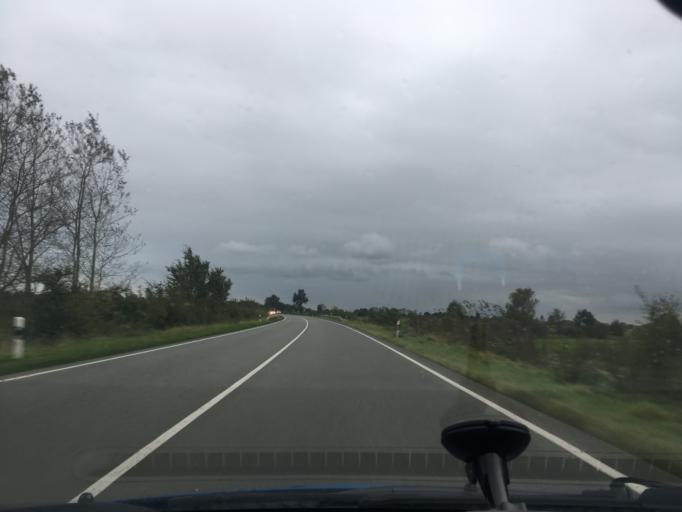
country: DE
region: Lower Saxony
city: Marschacht
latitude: 53.3956
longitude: 10.3329
